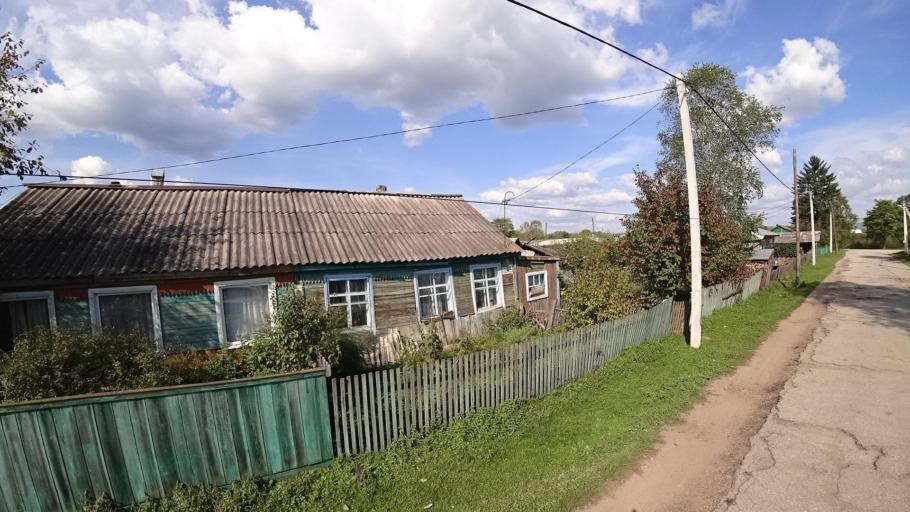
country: RU
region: Jewish Autonomous Oblast
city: Birakan
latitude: 48.9879
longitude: 131.7236
